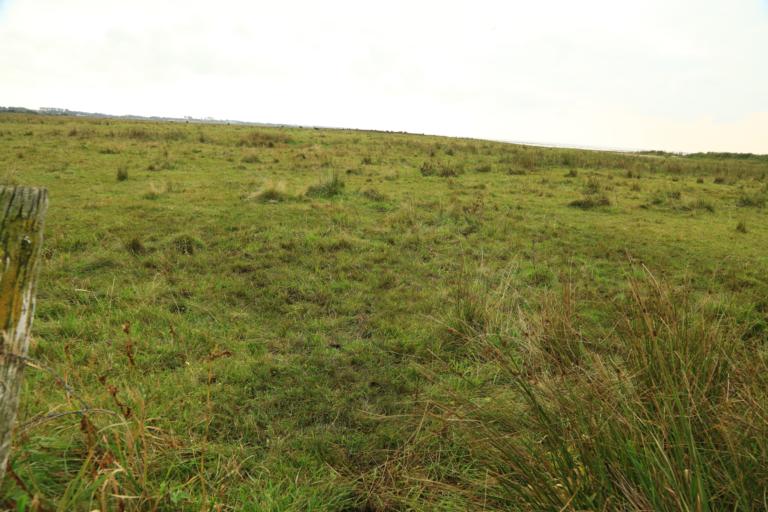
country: SE
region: Halland
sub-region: Varbergs Kommun
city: Tvaaker
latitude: 57.0049
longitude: 12.3531
